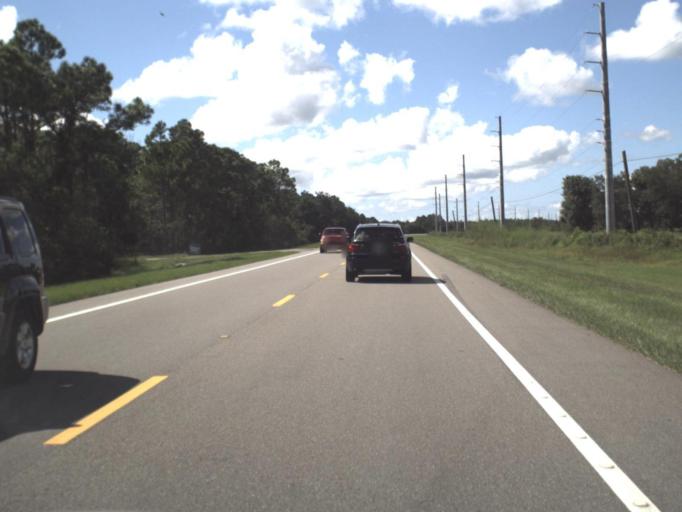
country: US
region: Florida
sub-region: Sarasota County
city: The Meadows
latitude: 27.4174
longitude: -82.3584
